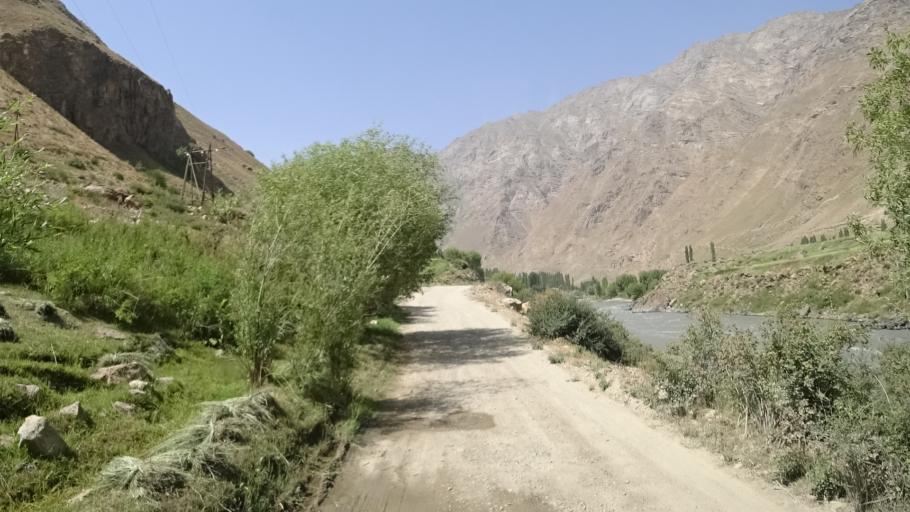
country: TJ
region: Gorno-Badakhshan
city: Khorugh
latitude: 37.1839
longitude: 71.4614
